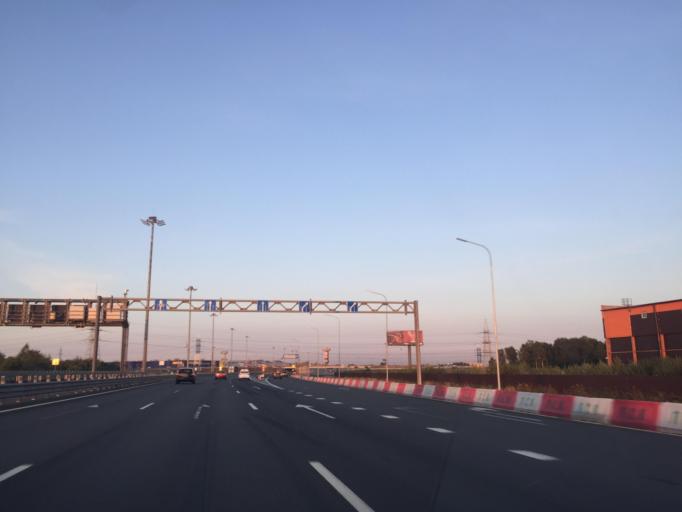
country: RU
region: Leningrad
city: Parnas
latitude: 60.0939
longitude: 30.3565
